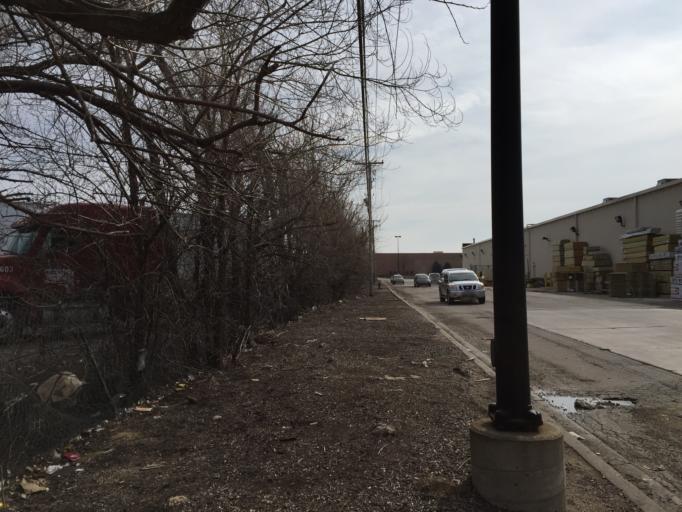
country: US
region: Illinois
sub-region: Cook County
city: Cicero
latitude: 41.8420
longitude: -87.7405
